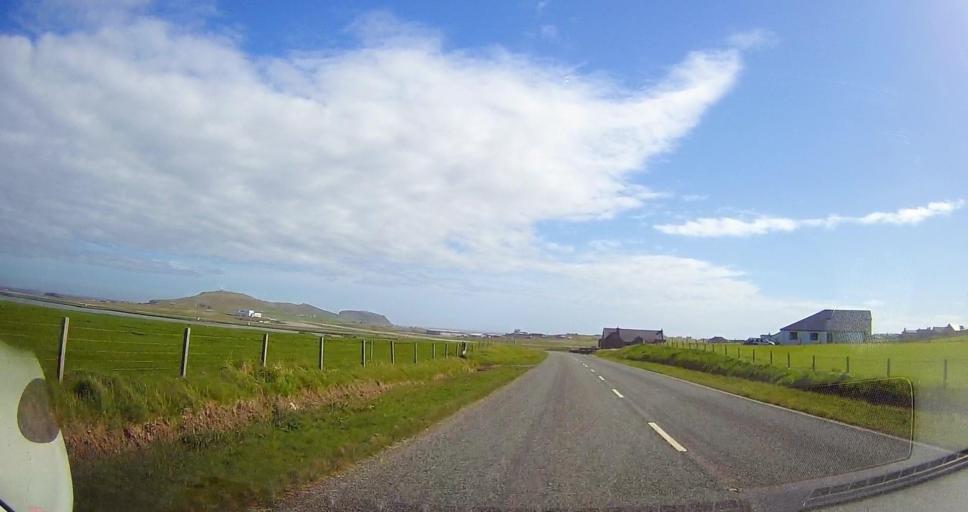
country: GB
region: Scotland
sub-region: Shetland Islands
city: Sandwick
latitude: 59.8890
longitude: -1.3033
